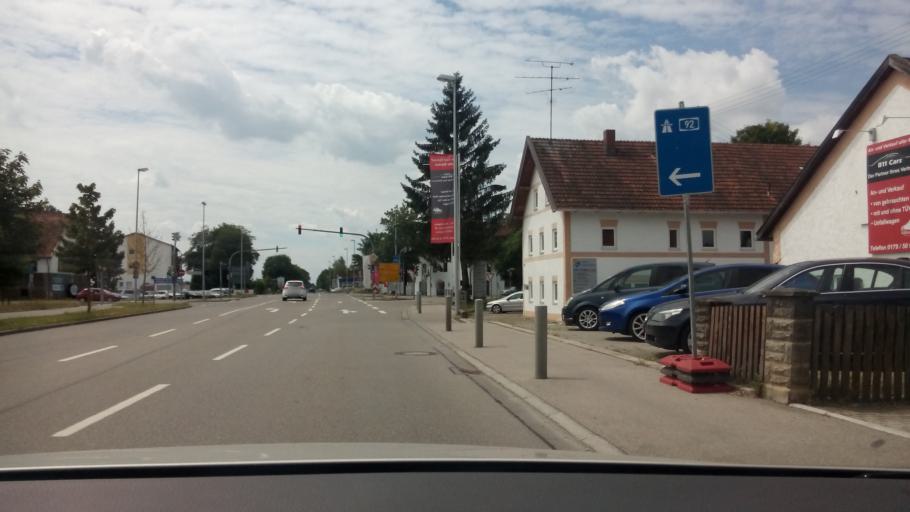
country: DE
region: Bavaria
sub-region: Upper Bavaria
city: Neufahrn bei Freising
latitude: 48.3165
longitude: 11.6904
